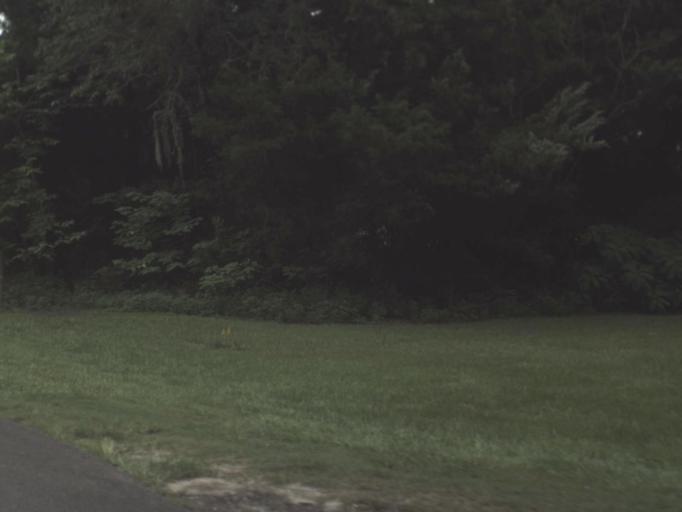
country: US
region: Florida
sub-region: Alachua County
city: Archer
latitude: 29.4929
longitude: -82.4942
